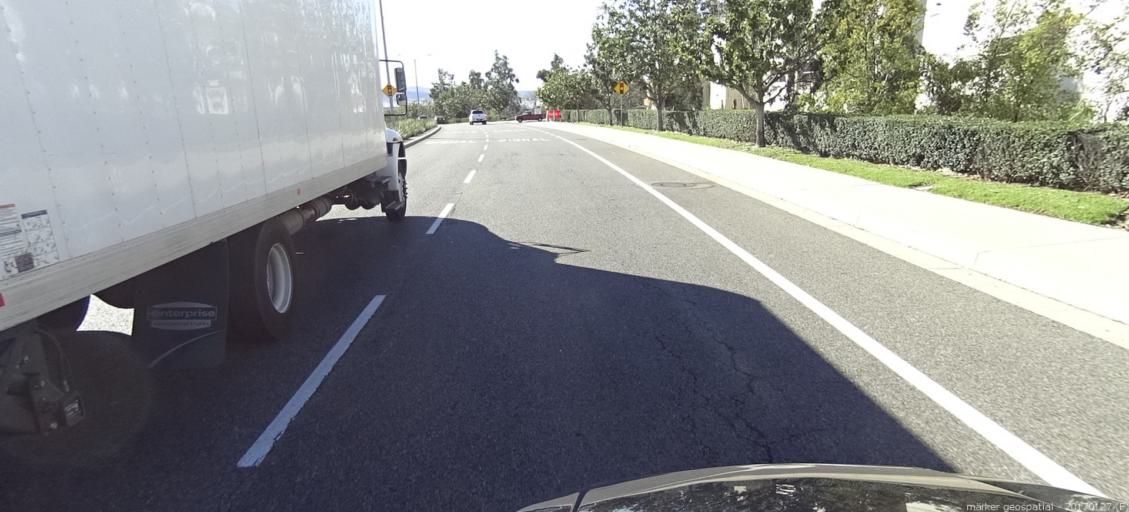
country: US
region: California
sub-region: Orange County
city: Lake Forest
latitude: 33.6677
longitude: -117.6828
